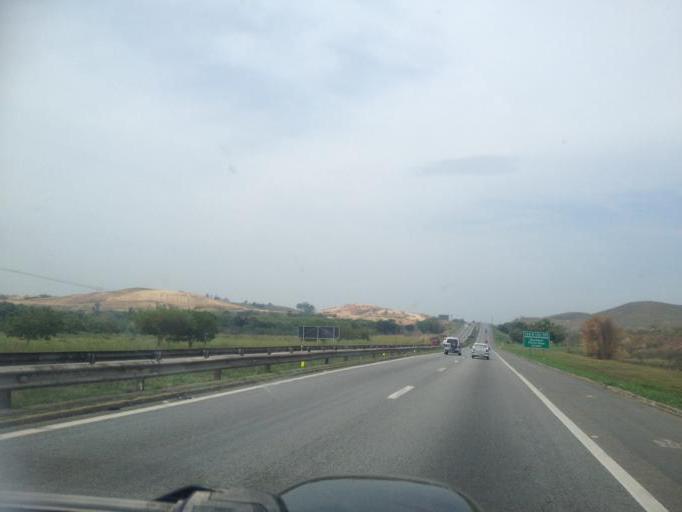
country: BR
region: Rio de Janeiro
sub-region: Porto Real
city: Porto Real
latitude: -22.4507
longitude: -44.3368
